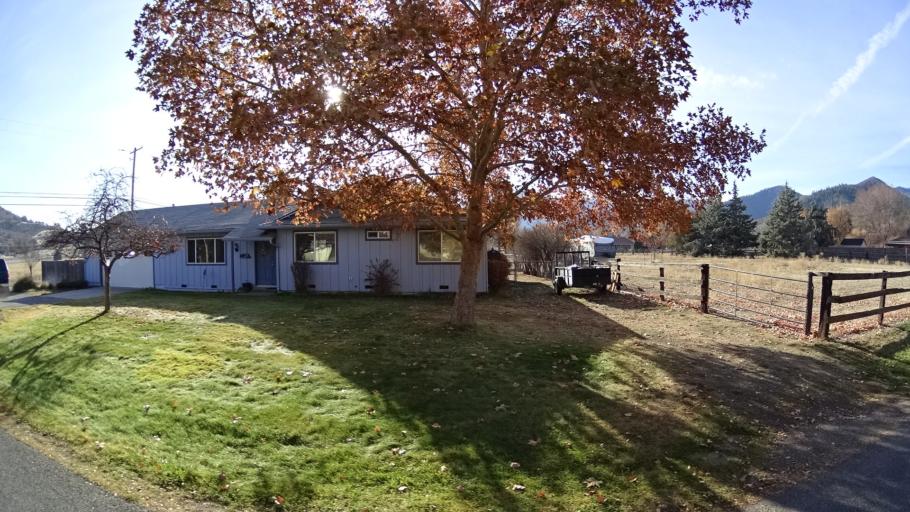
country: US
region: California
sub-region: Siskiyou County
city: Yreka
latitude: 41.6815
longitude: -122.6357
